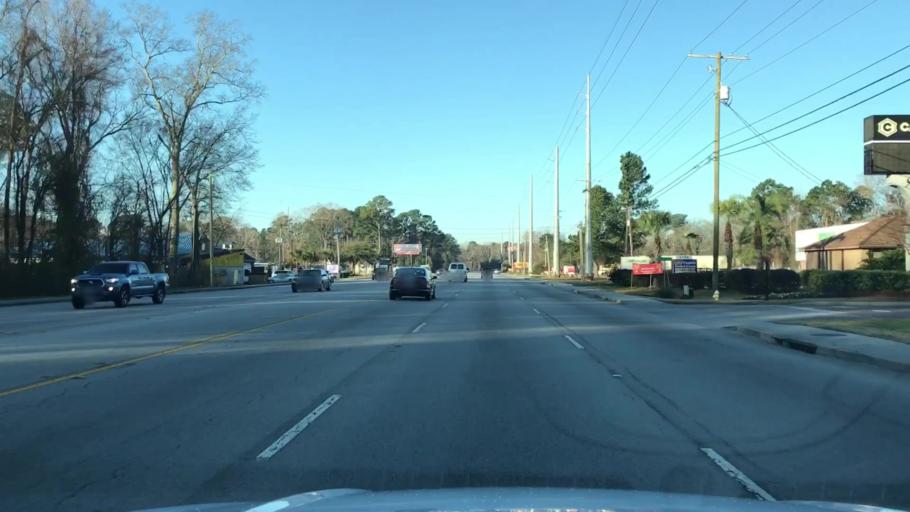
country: US
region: South Carolina
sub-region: Berkeley County
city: Ladson
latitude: 32.9233
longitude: -80.0918
